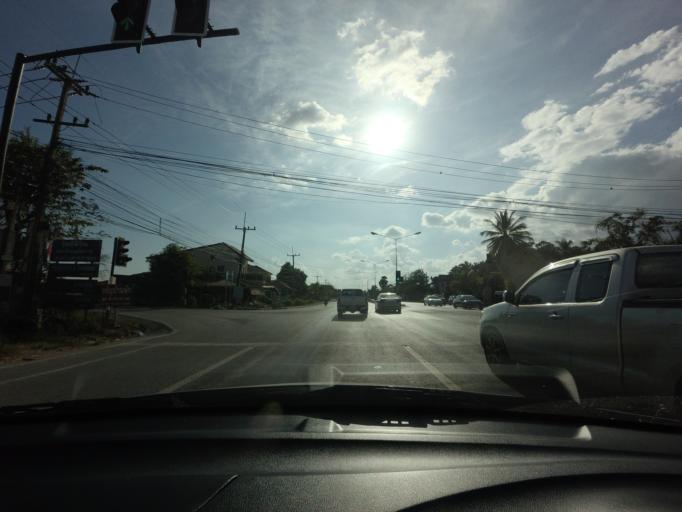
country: TH
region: Nakhon Nayok
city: Nakhon Nayok
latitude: 14.2572
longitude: 101.2629
